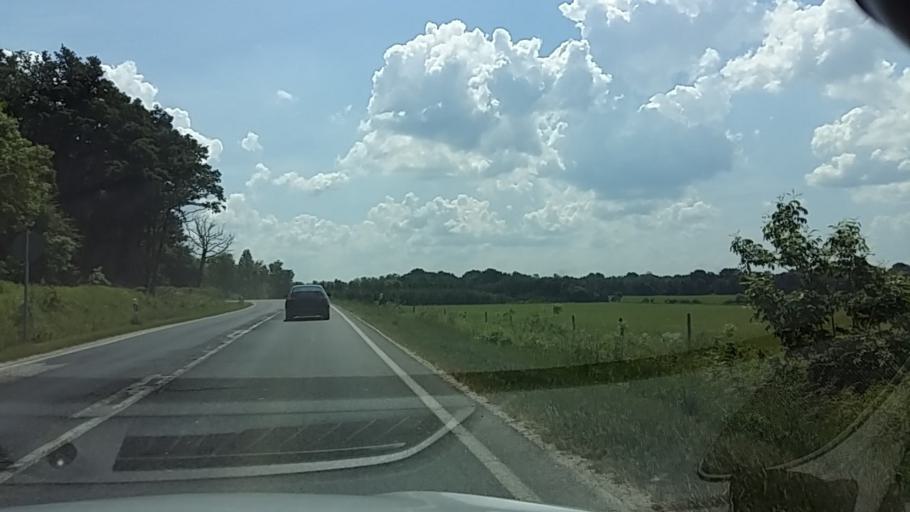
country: AT
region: Burgenland
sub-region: Politischer Bezirk Gussing
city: Heiligenbrunn
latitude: 46.9717
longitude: 16.3932
